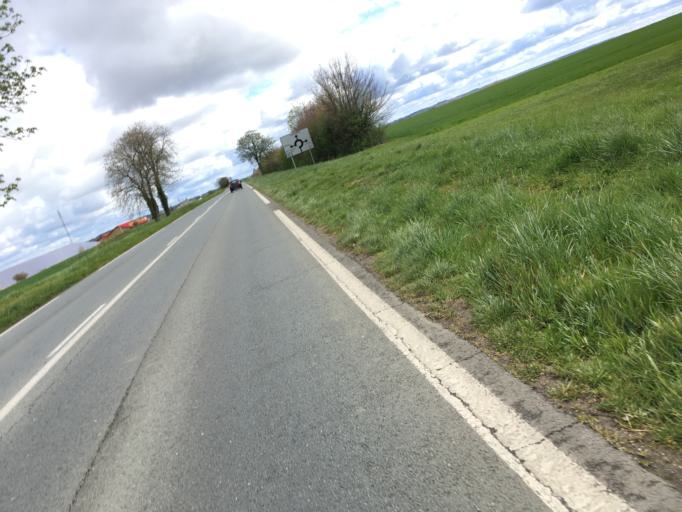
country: FR
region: Poitou-Charentes
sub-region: Departement de la Charente-Maritime
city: Saint-Germain-de-Marencennes
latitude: 46.1073
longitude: -0.7878
